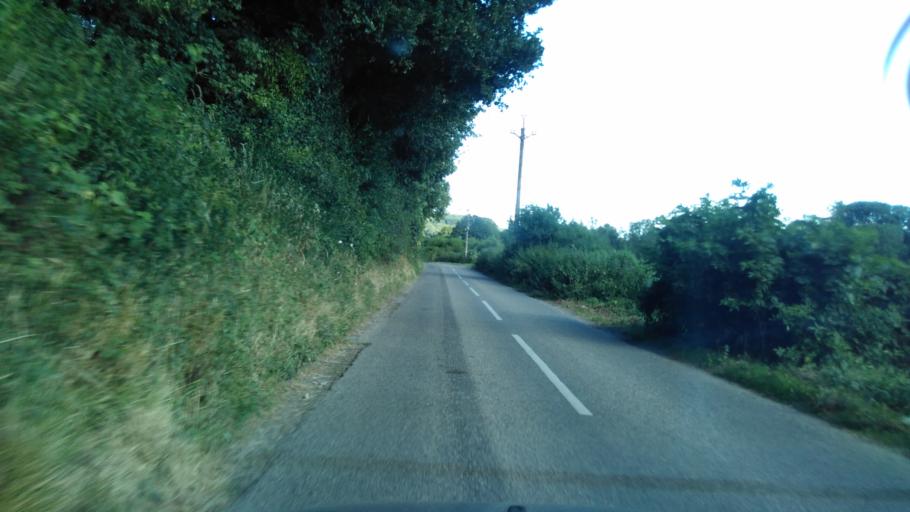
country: GB
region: England
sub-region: Kent
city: Dunkirk
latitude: 51.2478
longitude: 0.9636
